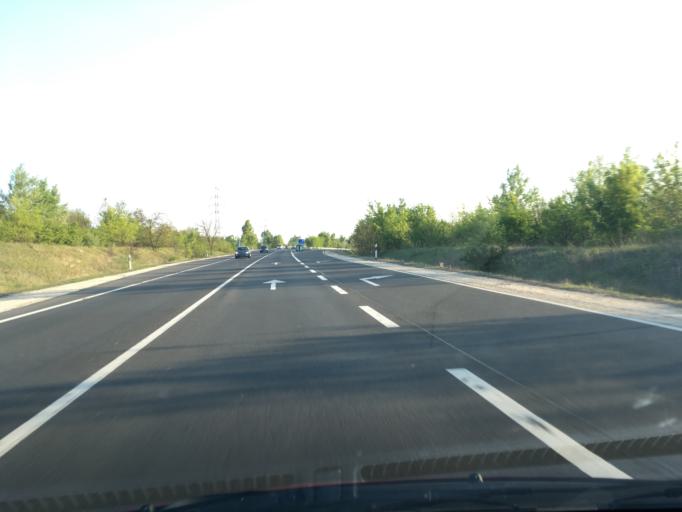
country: HU
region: Pest
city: Szod
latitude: 47.7515
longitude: 19.1785
